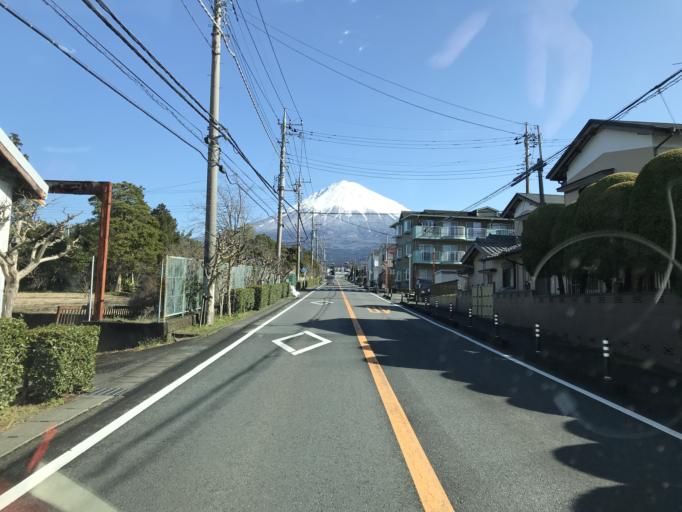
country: JP
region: Shizuoka
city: Fujinomiya
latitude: 35.2468
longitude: 138.6250
